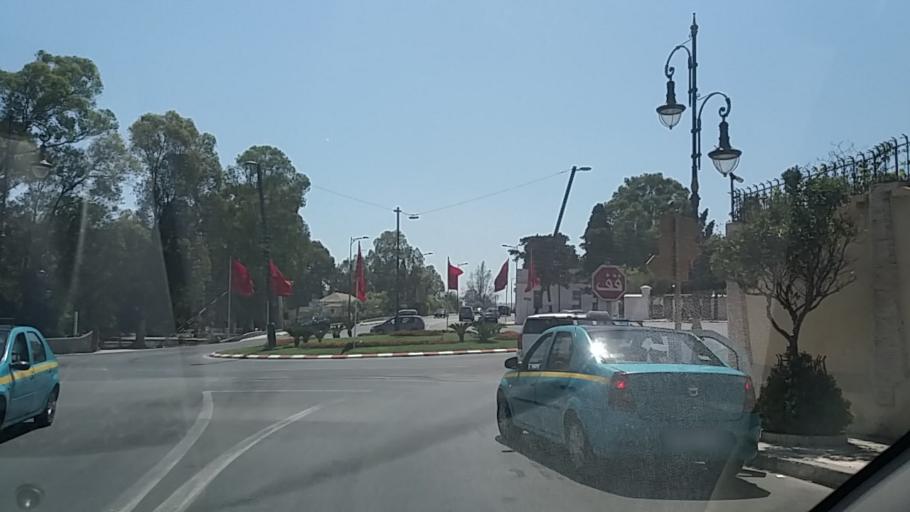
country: MA
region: Tanger-Tetouan
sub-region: Tanger-Assilah
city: Tangier
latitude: 35.7814
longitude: -5.8423
